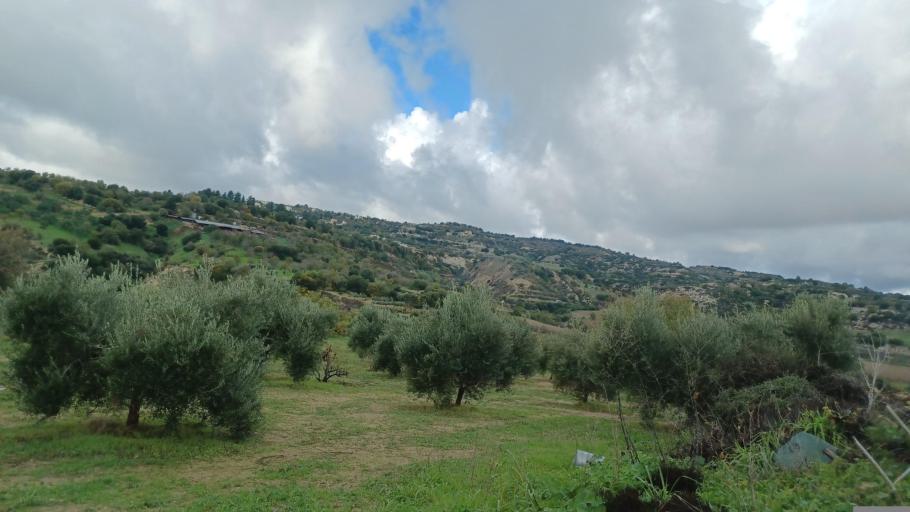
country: CY
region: Pafos
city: Mesogi
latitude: 34.8466
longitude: 32.5135
